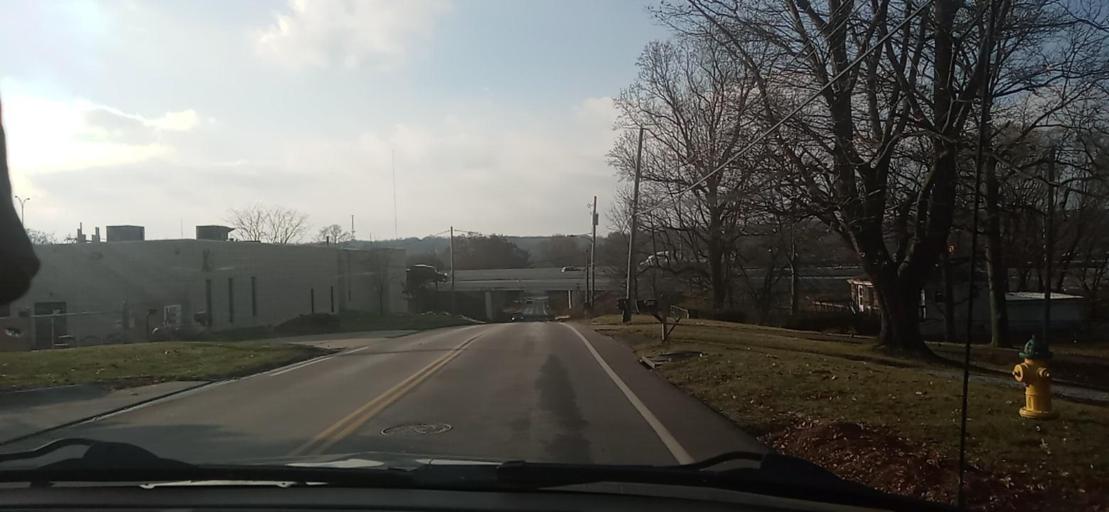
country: US
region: Ohio
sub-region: Summit County
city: Akron
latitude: 41.0587
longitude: -81.5657
